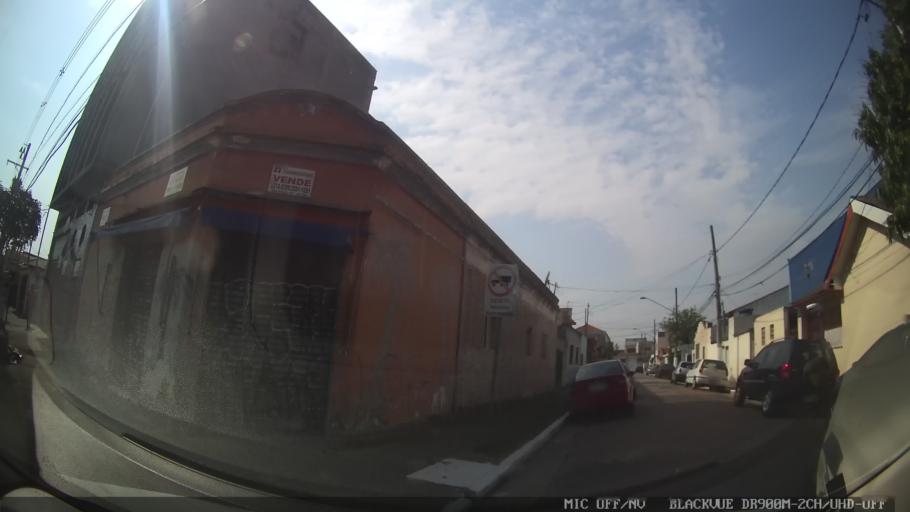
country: BR
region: Sao Paulo
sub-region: Sao Caetano Do Sul
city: Sao Caetano do Sul
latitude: -23.5941
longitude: -46.5943
